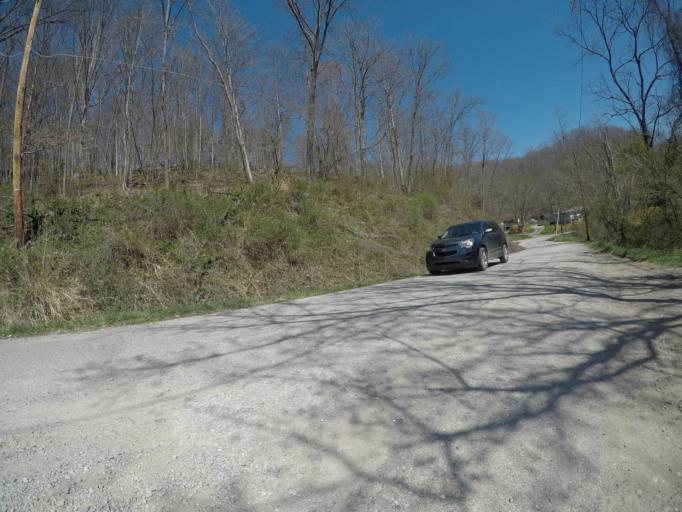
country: US
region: West Virginia
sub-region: Kanawha County
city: Charleston
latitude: 38.4178
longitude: -81.5839
